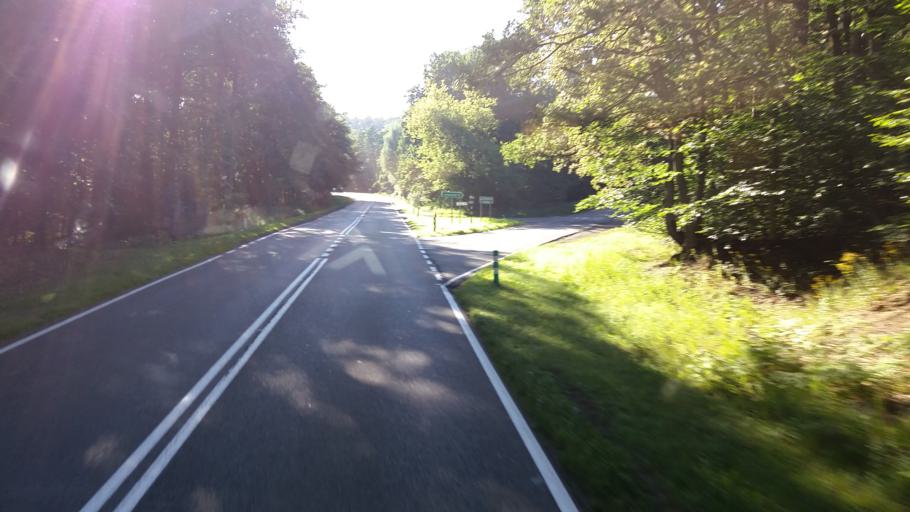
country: PL
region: West Pomeranian Voivodeship
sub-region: Powiat choszczenski
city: Drawno
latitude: 53.3044
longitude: 15.7689
